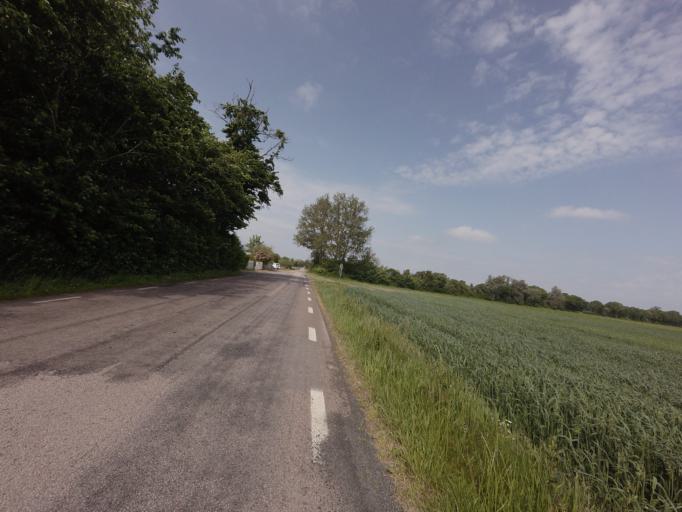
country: SE
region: Skane
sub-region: Hoganas Kommun
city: Hoganas
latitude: 56.1868
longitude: 12.6507
